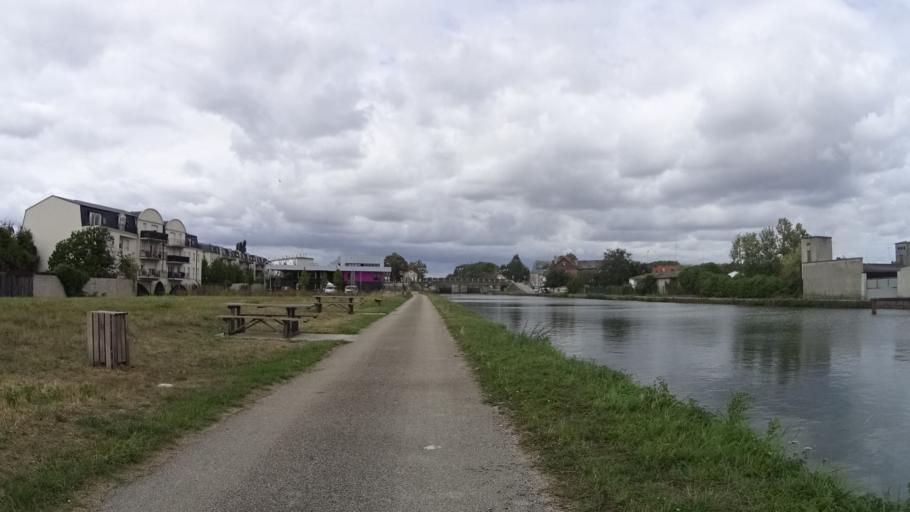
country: FR
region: Picardie
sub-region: Departement de l'Aisne
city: Tergnier
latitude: 49.6544
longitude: 3.3028
